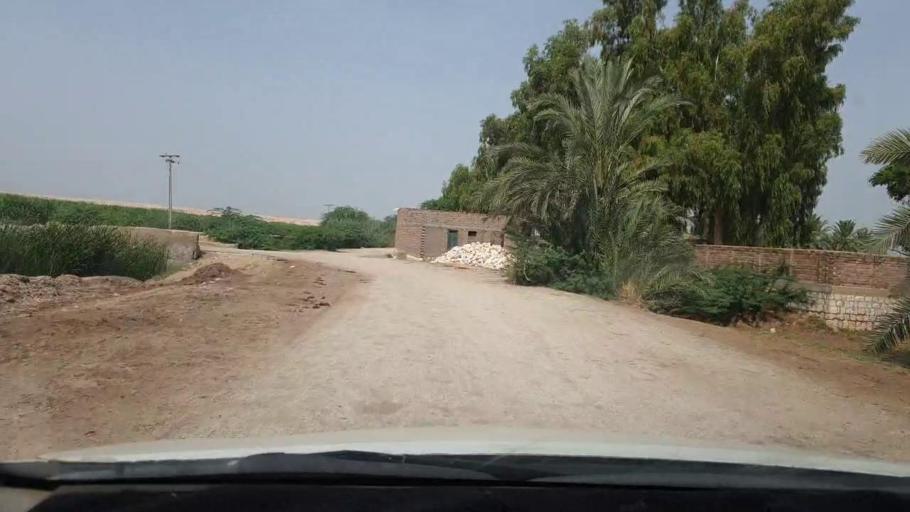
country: PK
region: Sindh
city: Rohri
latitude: 27.5961
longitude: 68.9822
